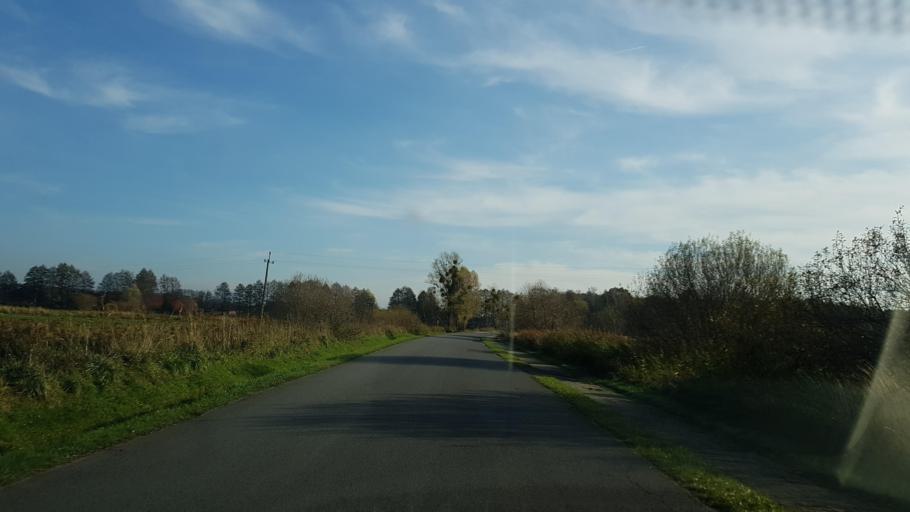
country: PL
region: West Pomeranian Voivodeship
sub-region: Powiat policki
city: Dobra
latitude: 53.4953
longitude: 14.3673
